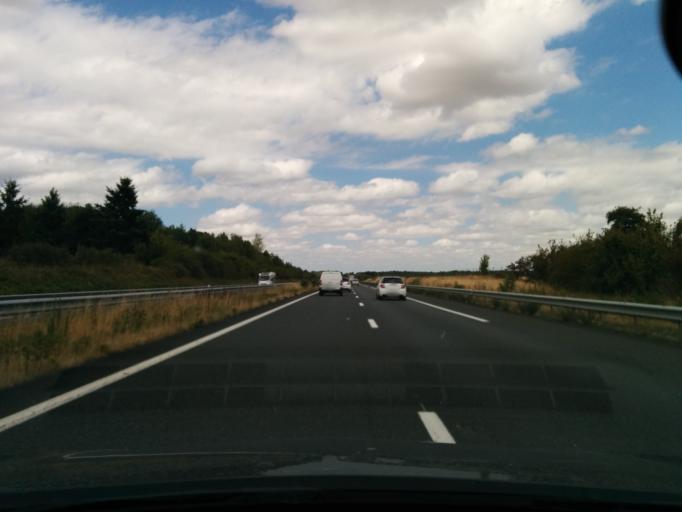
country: FR
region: Centre
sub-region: Departement de l'Indre
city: Luant
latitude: 46.6802
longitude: 1.5792
